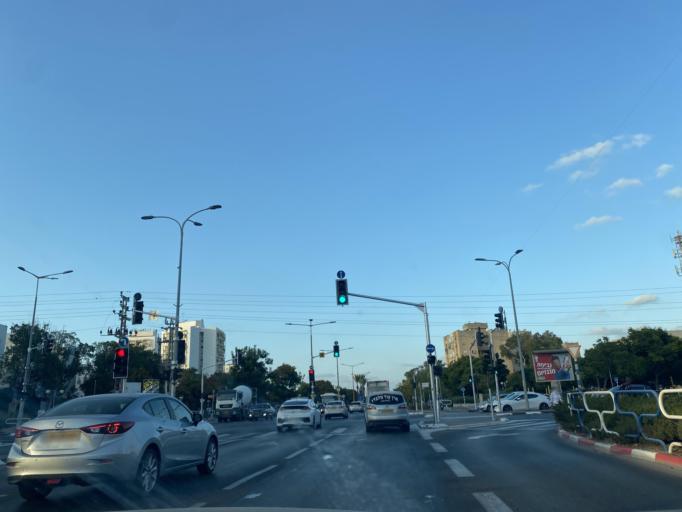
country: IL
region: Southern District
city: Ashdod
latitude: 31.7912
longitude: 34.6496
